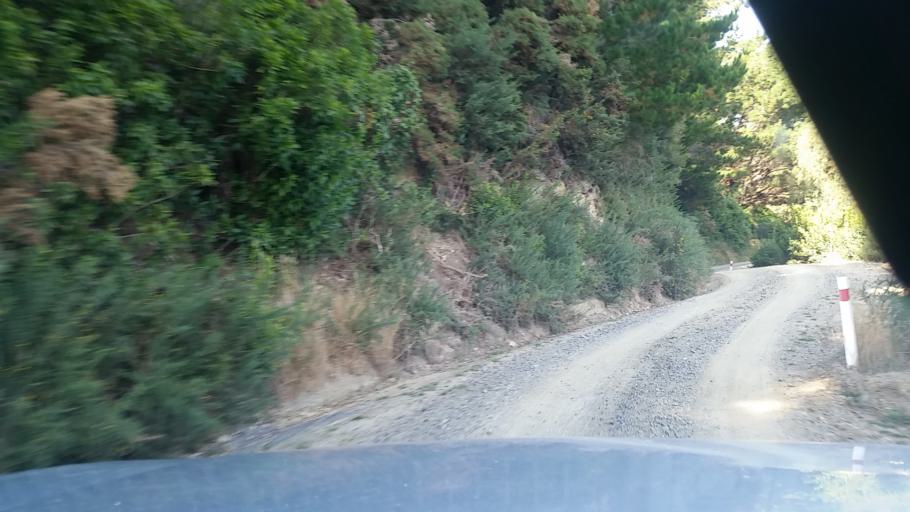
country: NZ
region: Marlborough
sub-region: Marlborough District
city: Picton
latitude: -41.2994
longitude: 174.1799
